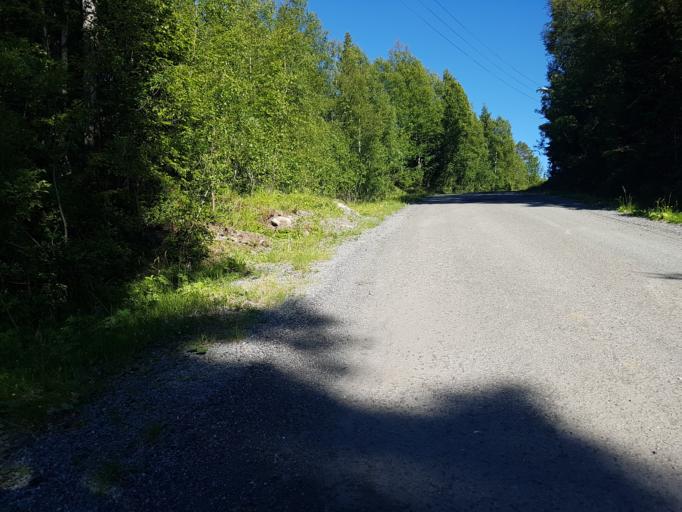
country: NO
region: Sor-Trondelag
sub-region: Trondheim
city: Trondheim
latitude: 63.4292
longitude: 10.2790
